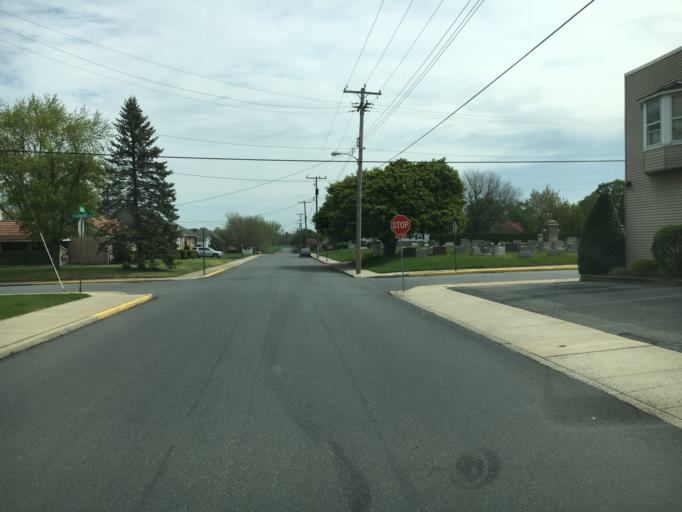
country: US
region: Pennsylvania
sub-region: Berks County
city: Fleetwood
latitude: 40.4573
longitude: -75.8174
